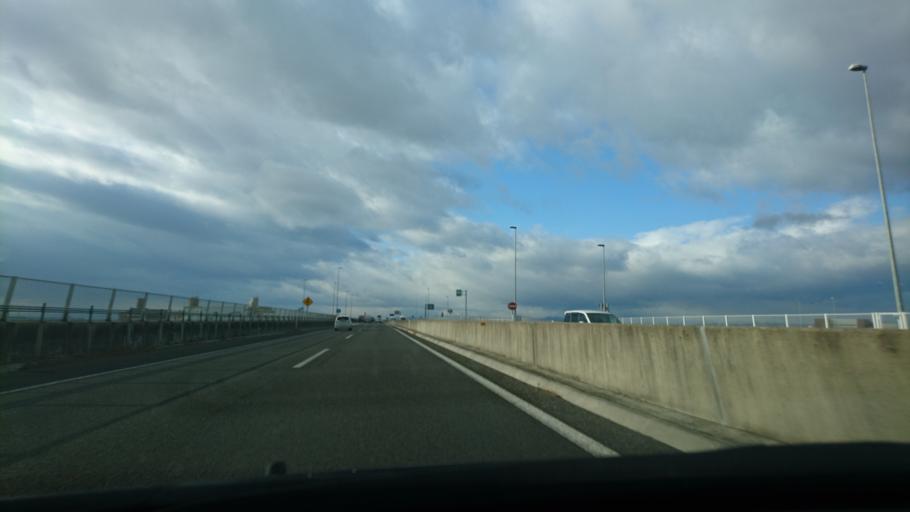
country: JP
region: Miyagi
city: Rifu
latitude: 38.2698
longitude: 140.9778
